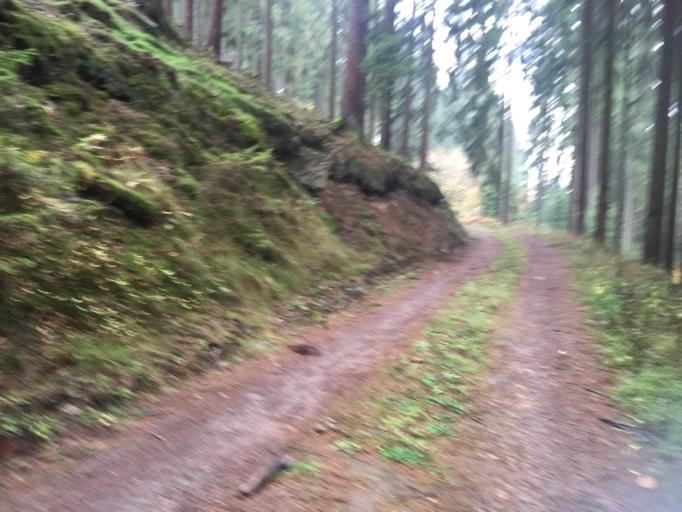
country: DE
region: Baden-Wuerttemberg
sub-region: Karlsruhe Region
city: Heddesbach
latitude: 49.4656
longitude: 8.8541
